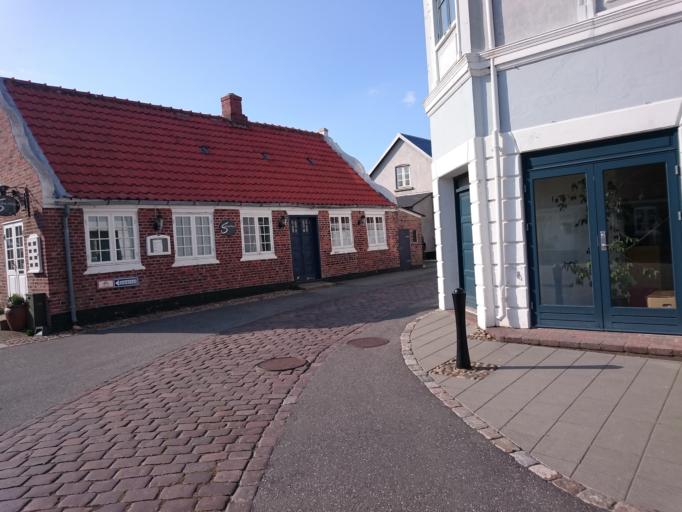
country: DK
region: South Denmark
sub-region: Fano Kommune
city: Nordby
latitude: 55.4476
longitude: 8.4060
